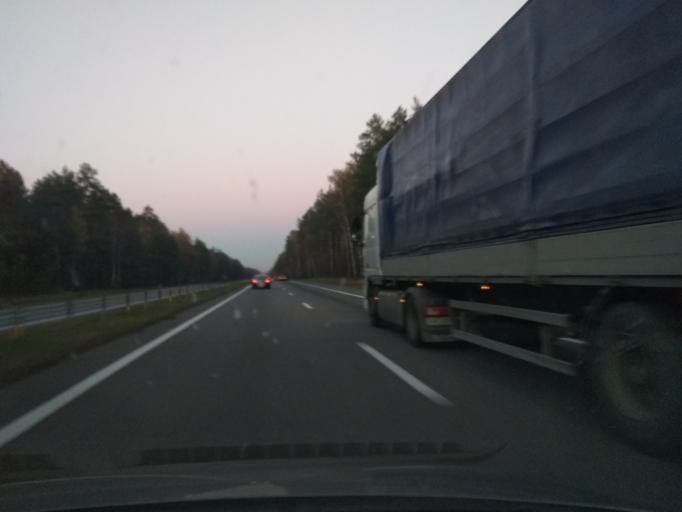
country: BY
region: Minsk
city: Enyerhyetykaw
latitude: 53.5590
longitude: 26.9773
